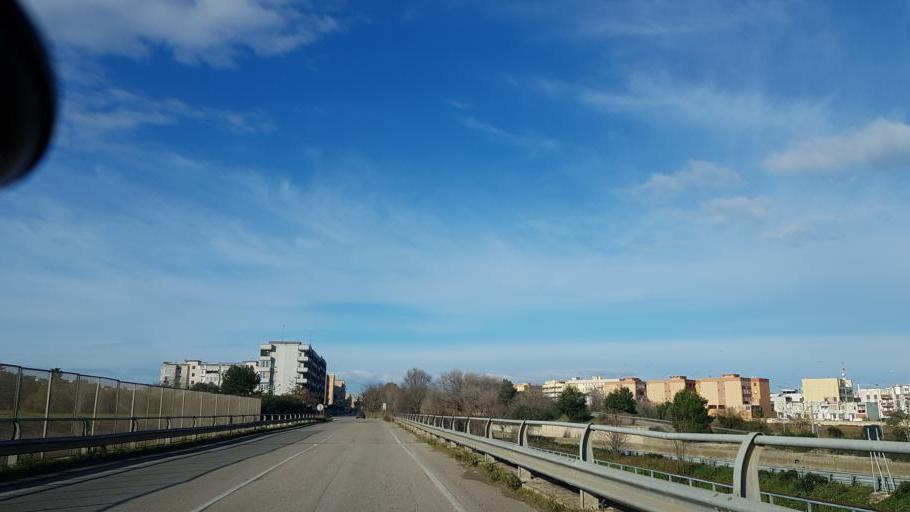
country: IT
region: Apulia
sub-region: Provincia di Brindisi
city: Brindisi
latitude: 40.6193
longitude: 17.9374
